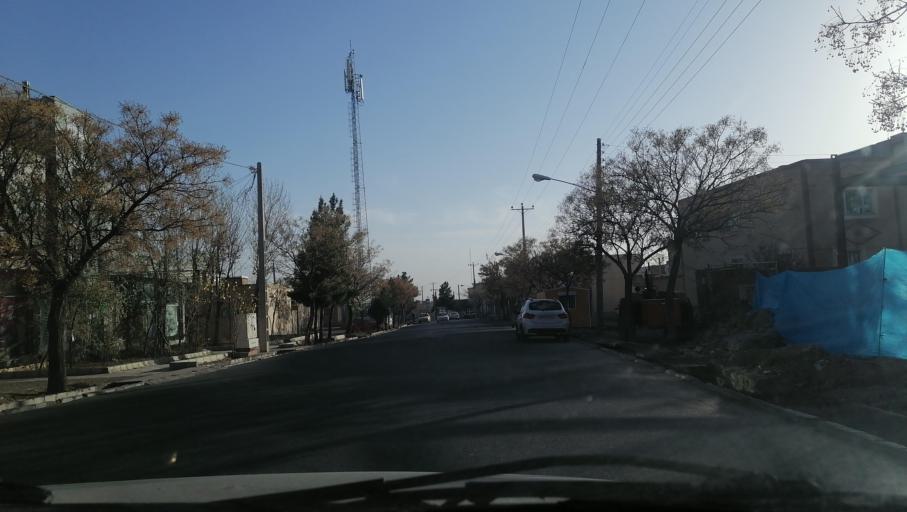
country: IR
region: Razavi Khorasan
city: Sabzevar
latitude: 36.2892
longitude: 57.6763
